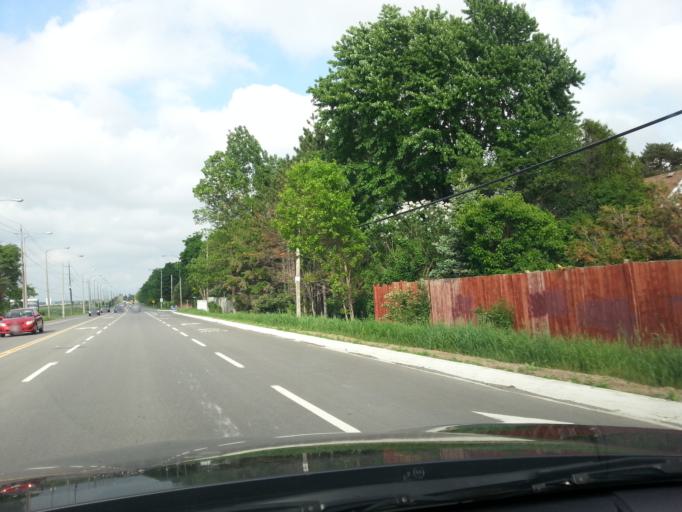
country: CA
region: Ontario
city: Bells Corners
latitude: 45.2831
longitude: -75.7686
